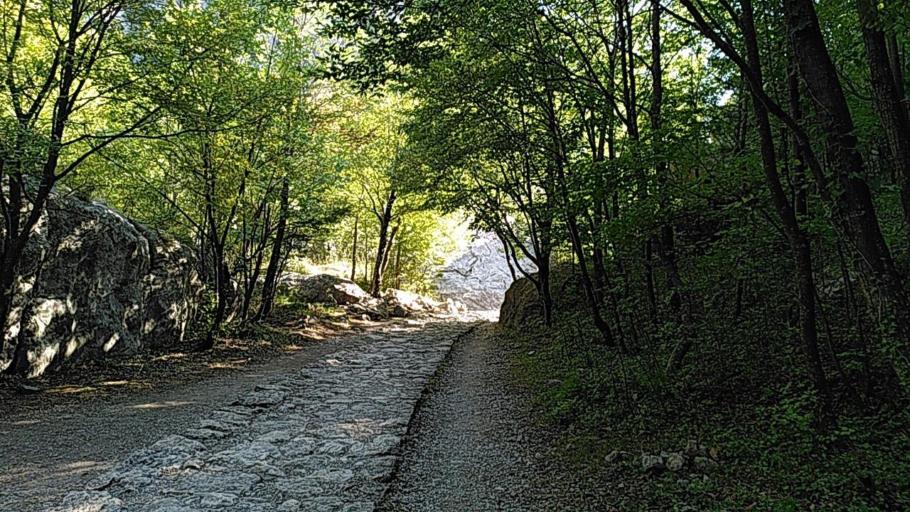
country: HR
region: Zadarska
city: Starigrad
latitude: 44.3094
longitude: 15.4793
